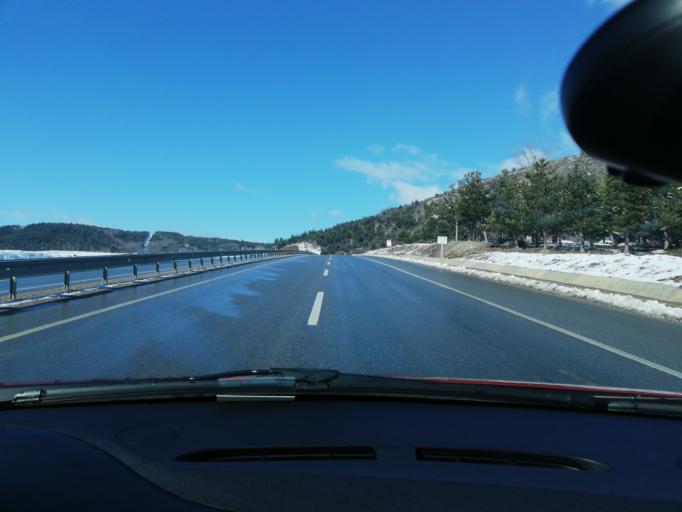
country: TR
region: Kastamonu
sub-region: Cide
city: Kastamonu
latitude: 41.3603
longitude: 33.6986
